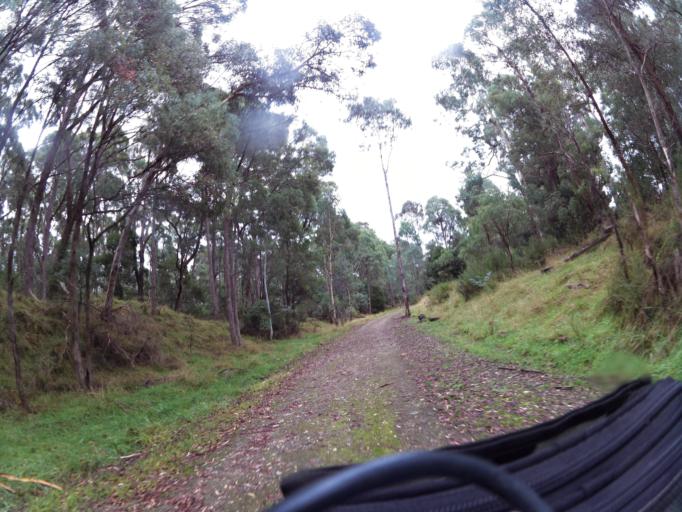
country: AU
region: New South Wales
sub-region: Greater Hume Shire
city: Holbrook
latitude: -36.1725
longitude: 147.4972
